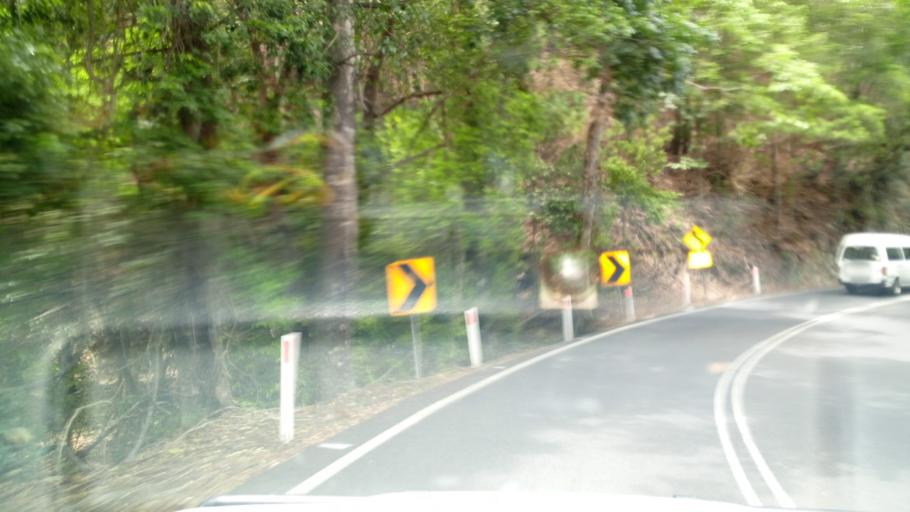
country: AU
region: Queensland
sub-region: Cairns
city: Redlynch
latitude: -16.8465
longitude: 145.6830
